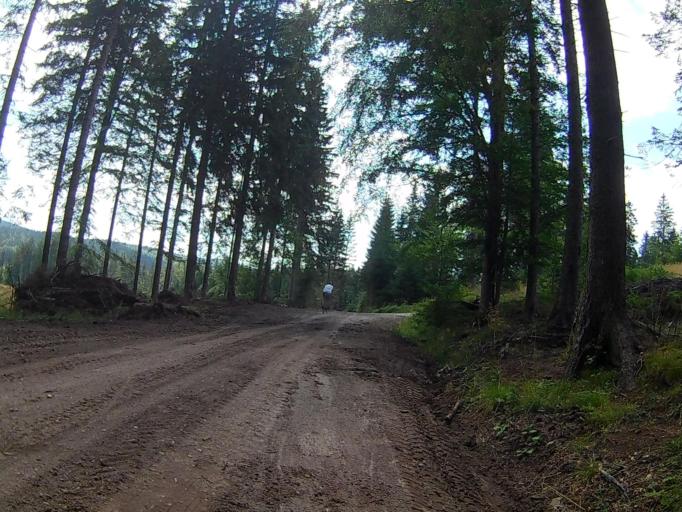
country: SI
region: Lovrenc na Pohorju
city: Lovrenc na Pohorju
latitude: 46.4839
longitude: 15.4424
